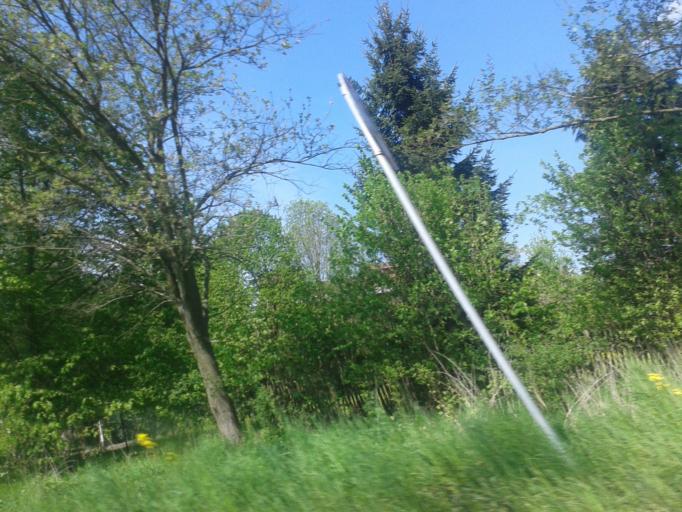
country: CZ
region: Central Bohemia
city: Lochovice
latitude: 49.8436
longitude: 13.9747
